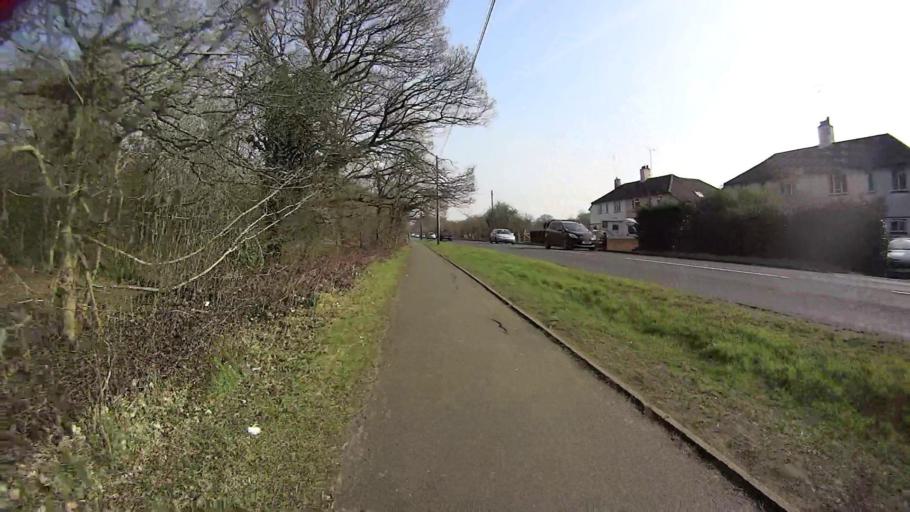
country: GB
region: England
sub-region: Surrey
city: Salfords
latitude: 51.2195
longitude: -0.1833
